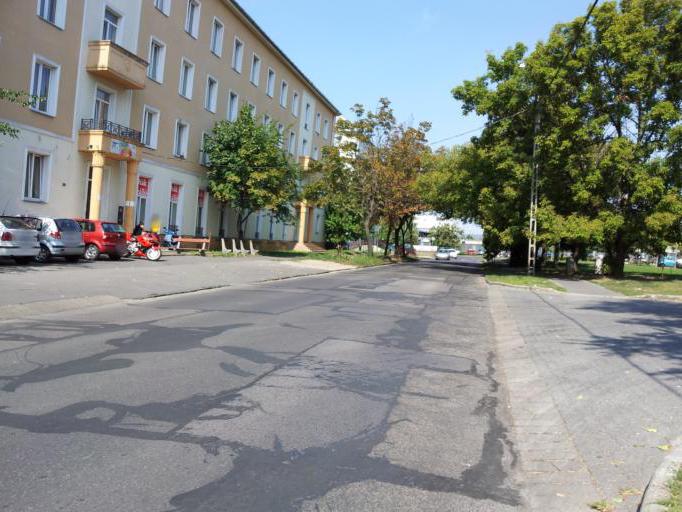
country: HU
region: Budapest
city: Budapest XIV. keruelet
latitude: 47.5055
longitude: 19.1150
